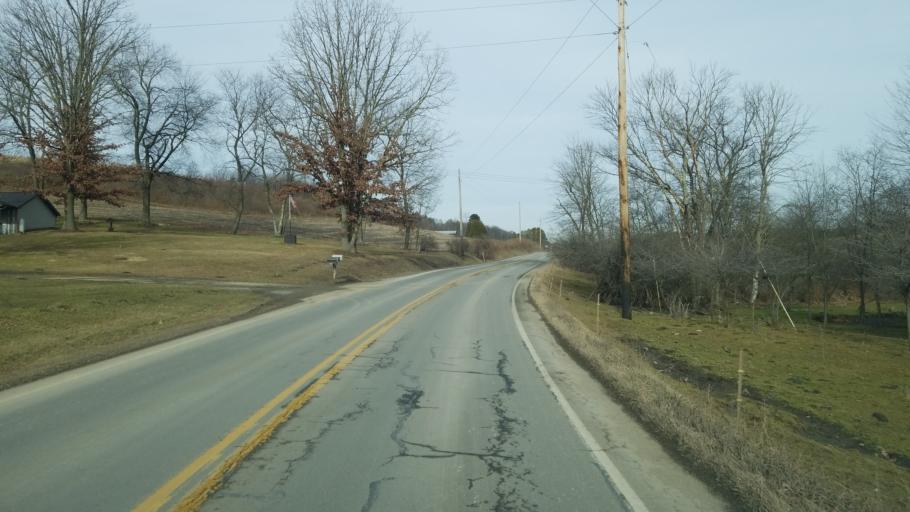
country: US
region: Pennsylvania
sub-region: Jefferson County
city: Punxsutawney
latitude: 40.8931
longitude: -79.0426
